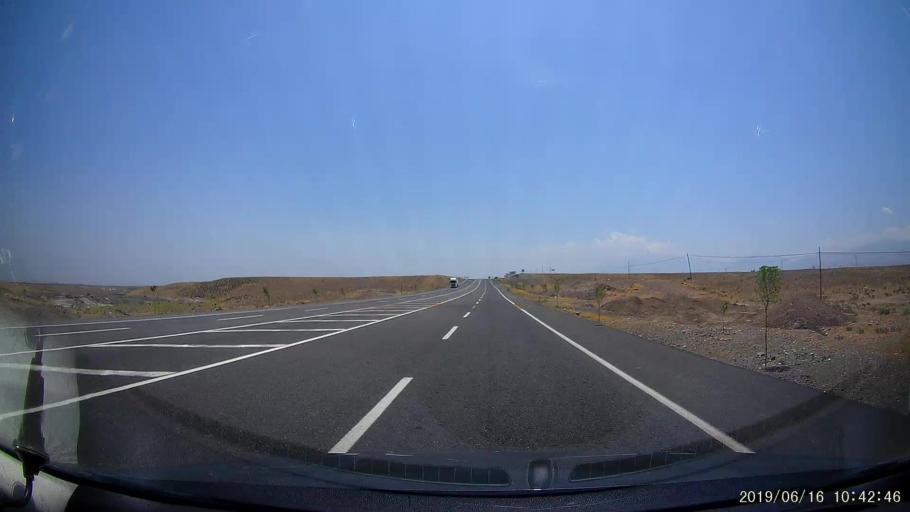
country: AM
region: Armavir
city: Shenavan
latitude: 40.0398
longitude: 43.8139
